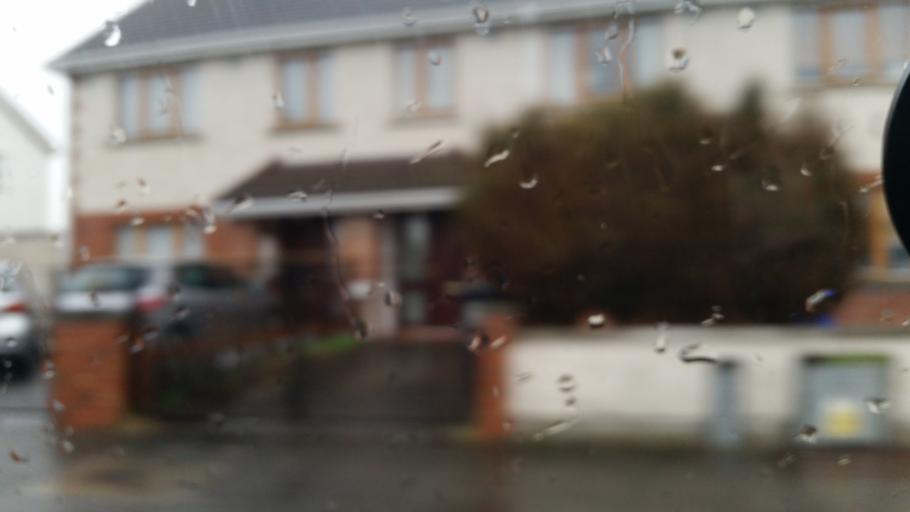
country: IE
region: Leinster
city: Hartstown
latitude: 53.3934
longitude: -6.4054
